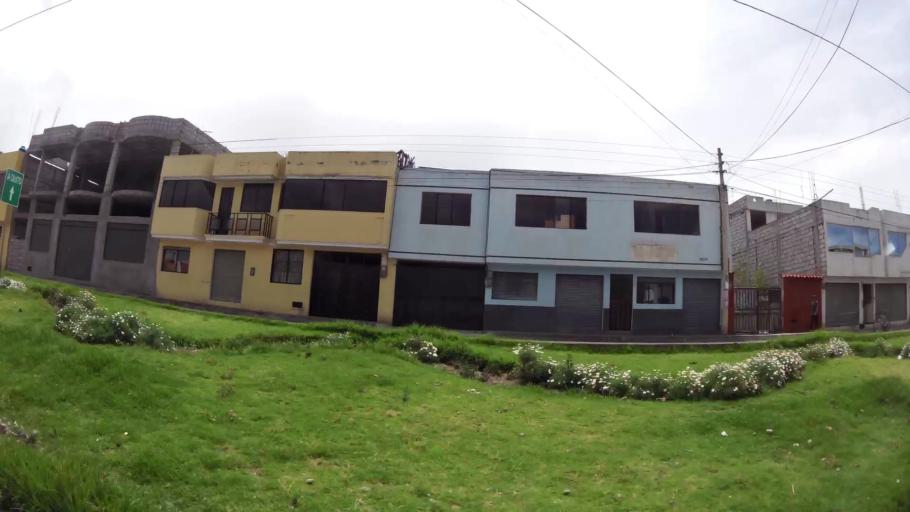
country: EC
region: Cotopaxi
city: San Miguel de Salcedo
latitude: -1.0471
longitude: -78.5876
